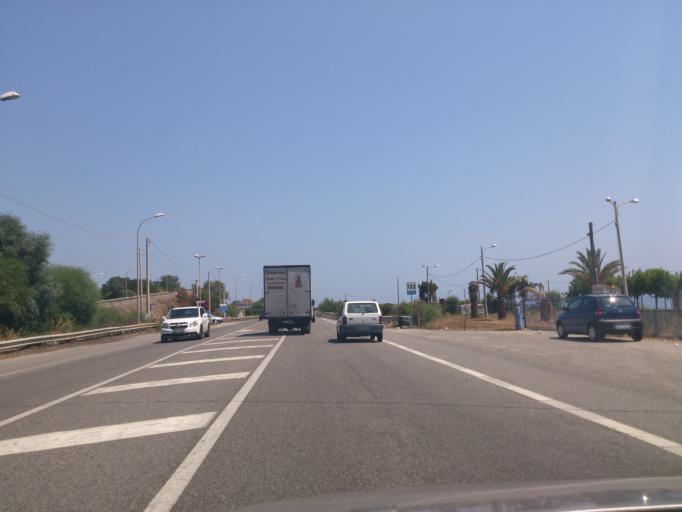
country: IT
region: Calabria
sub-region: Provincia di Reggio Calabria
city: Monasterace Marina
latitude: 38.4167
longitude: 16.5600
